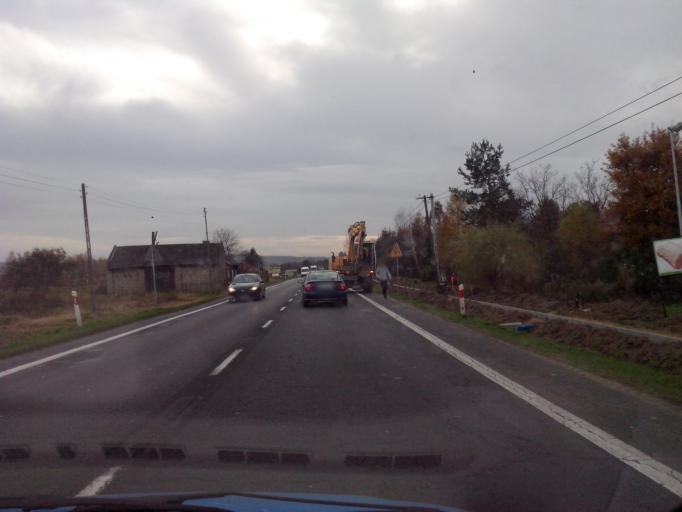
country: PL
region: Subcarpathian Voivodeship
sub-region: Powiat rzeszowski
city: Lutoryz
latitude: 49.9557
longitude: 21.9157
